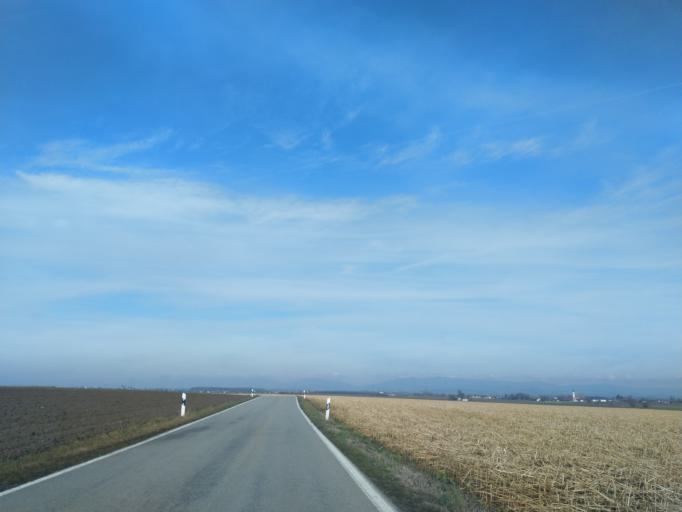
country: DE
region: Bavaria
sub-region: Lower Bavaria
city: Buchhofen
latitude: 48.6722
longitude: 12.9359
